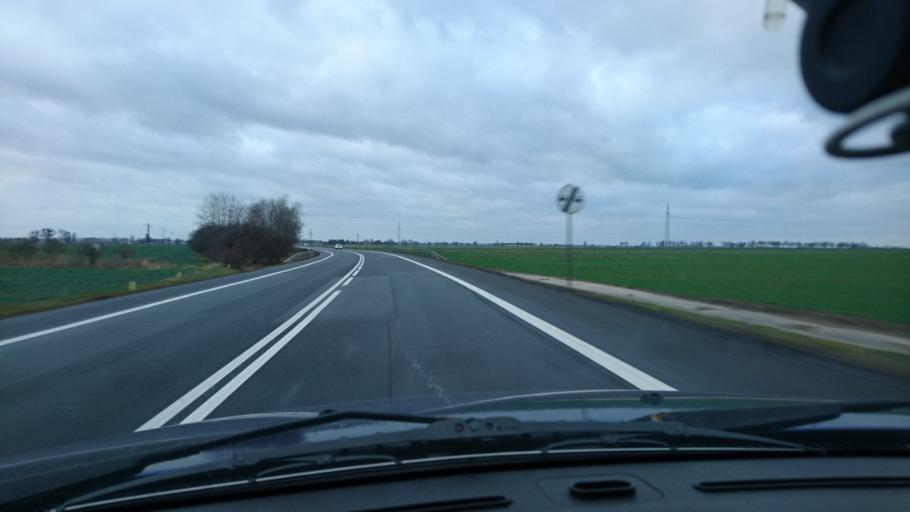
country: PL
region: Opole Voivodeship
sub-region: Powiat kluczborski
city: Kluczbork
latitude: 50.9889
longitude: 18.2338
